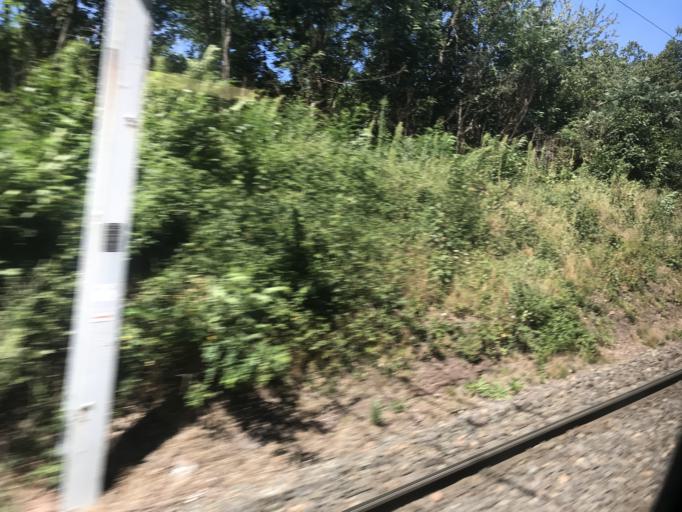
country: FR
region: Alsace
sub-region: Departement du Bas-Rhin
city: Saverne
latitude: 48.7243
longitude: 7.3257
